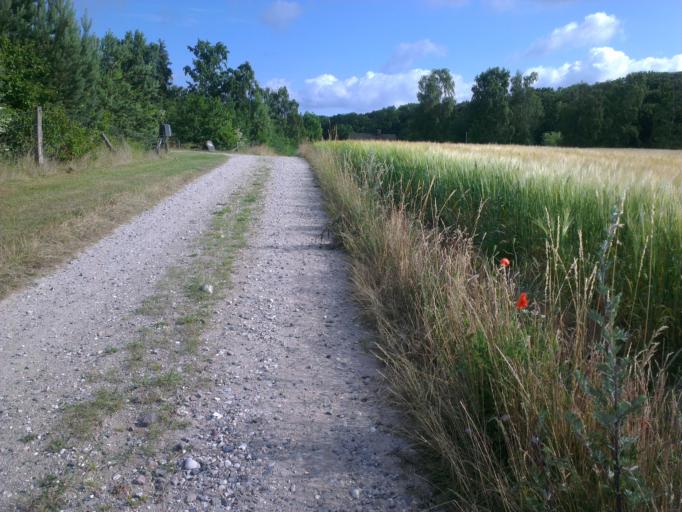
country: DK
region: Capital Region
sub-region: Frederikssund Kommune
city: Jaegerspris
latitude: 55.8817
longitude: 11.9798
